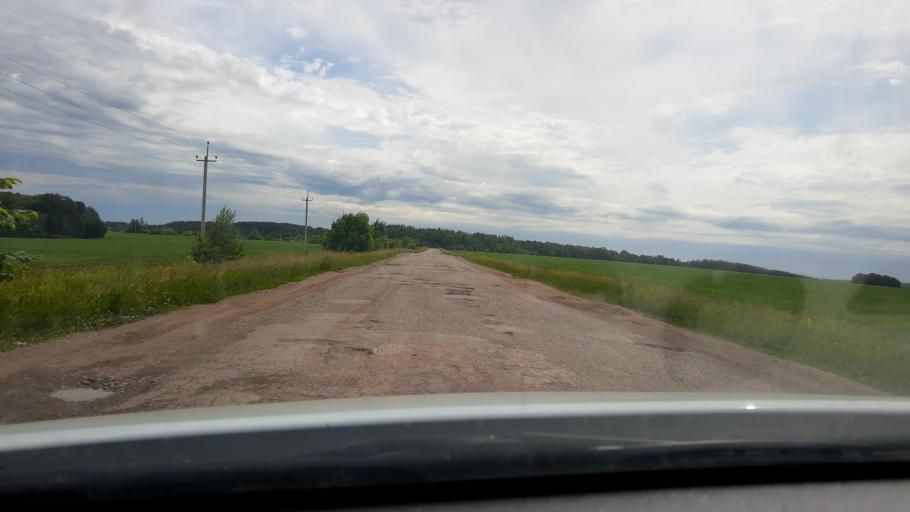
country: RU
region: Bashkortostan
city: Iglino
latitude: 54.7538
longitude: 56.5298
